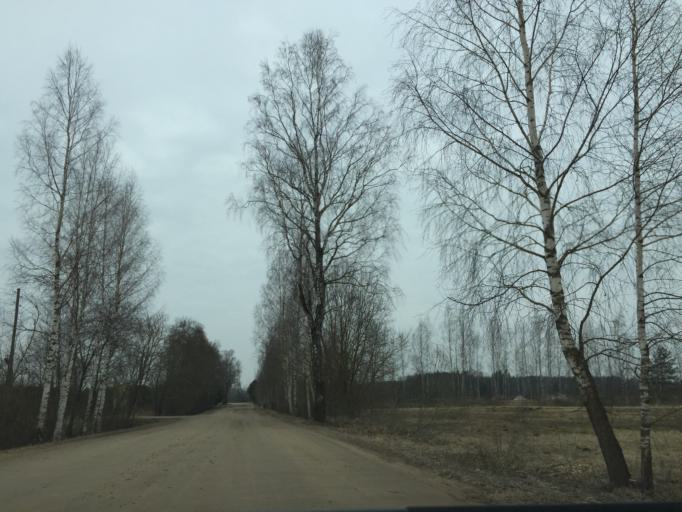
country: LV
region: Kekava
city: Kekava
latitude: 56.8059
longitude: 24.1712
